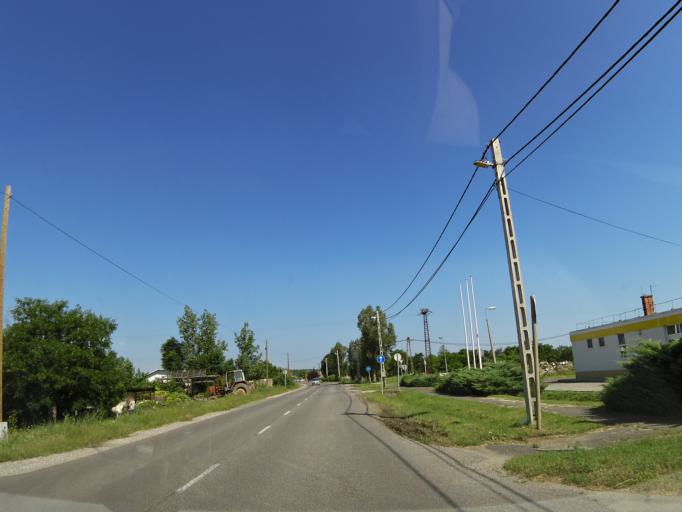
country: HU
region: Jasz-Nagykun-Szolnok
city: Toszeg
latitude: 47.0930
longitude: 20.1527
